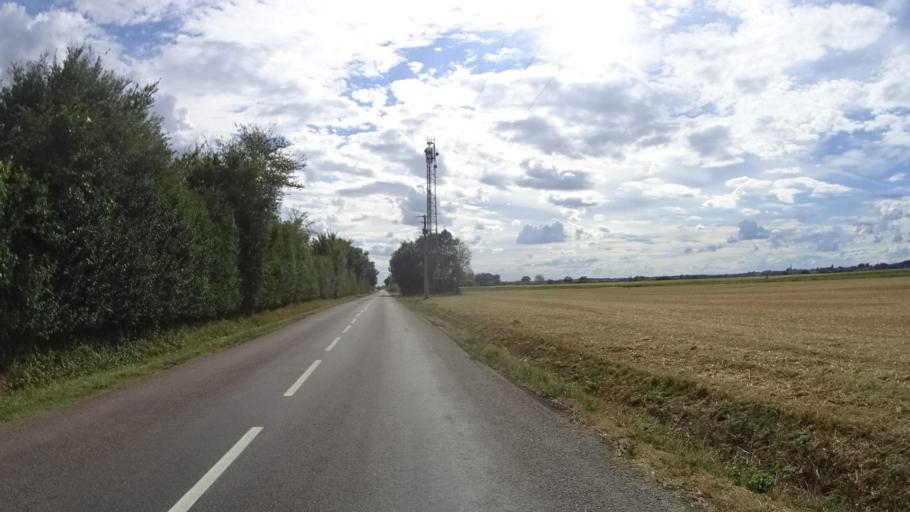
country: FR
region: Bourgogne
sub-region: Departement de la Cote-d'Or
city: Seurre
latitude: 46.9940
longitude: 5.1353
